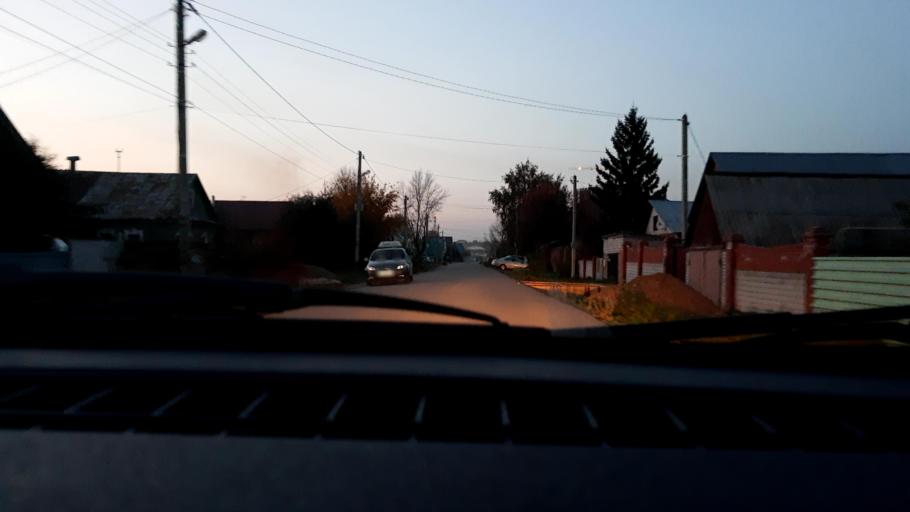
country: RU
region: Bashkortostan
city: Mikhaylovka
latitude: 54.7642
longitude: 55.9024
